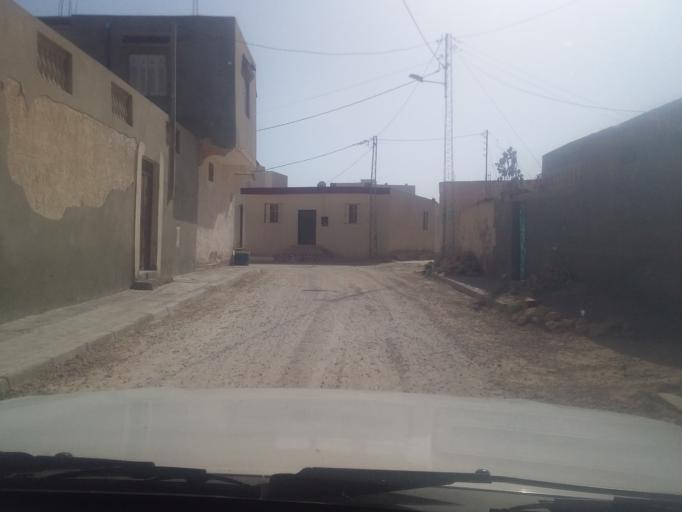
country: TN
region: Qabis
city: Gabes
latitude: 33.6222
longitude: 10.2860
